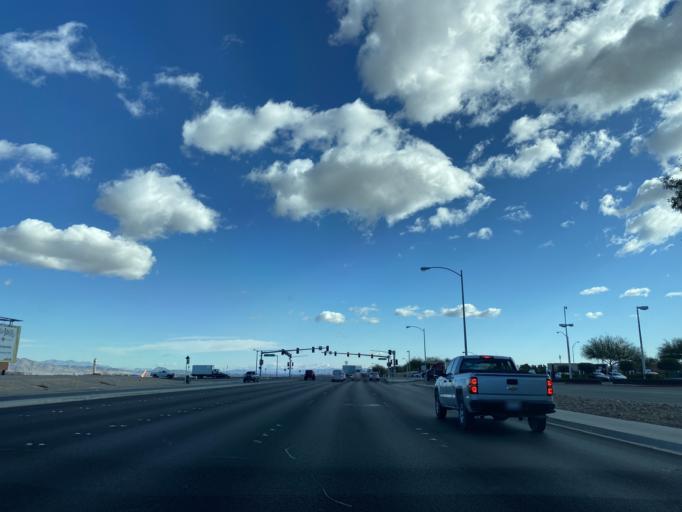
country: US
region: Nevada
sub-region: Clark County
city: Paradise
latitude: 36.0710
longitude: -115.1741
